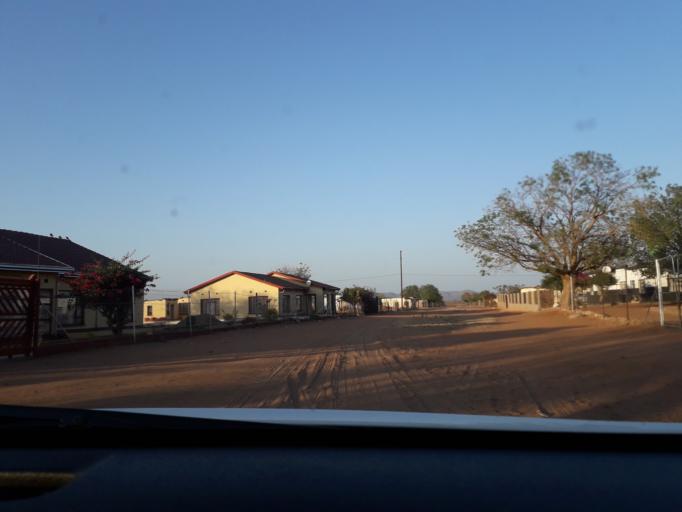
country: ZA
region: Limpopo
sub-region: Waterberg District Municipality
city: Mokopane
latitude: -23.9157
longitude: 28.8723
